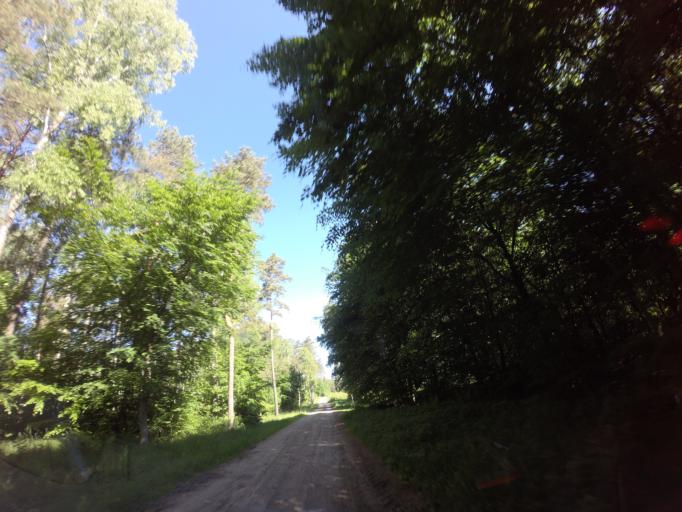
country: PL
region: West Pomeranian Voivodeship
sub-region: Powiat choszczenski
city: Drawno
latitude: 53.2271
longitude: 15.6747
